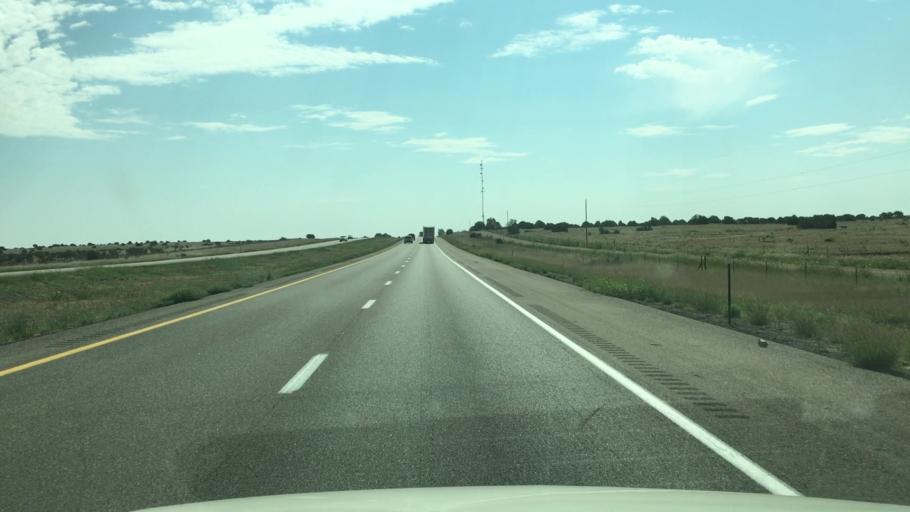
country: US
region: New Mexico
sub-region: Guadalupe County
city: Santa Rosa
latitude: 34.9730
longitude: -104.9264
